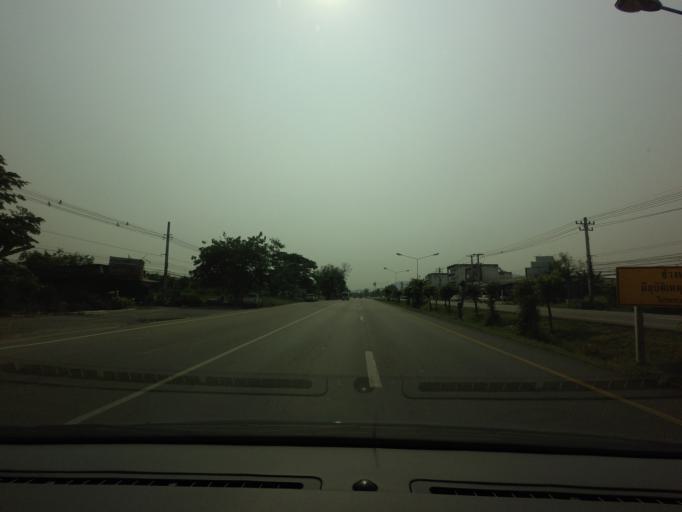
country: TH
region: Prachuap Khiri Khan
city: Pran Buri
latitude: 12.3777
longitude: 99.8900
